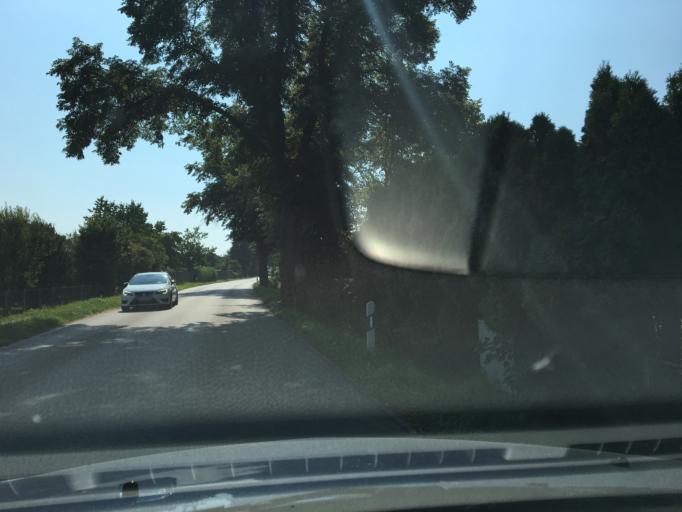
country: DE
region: Bavaria
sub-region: Upper Bavaria
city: Mettenheim
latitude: 48.2532
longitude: 12.4664
